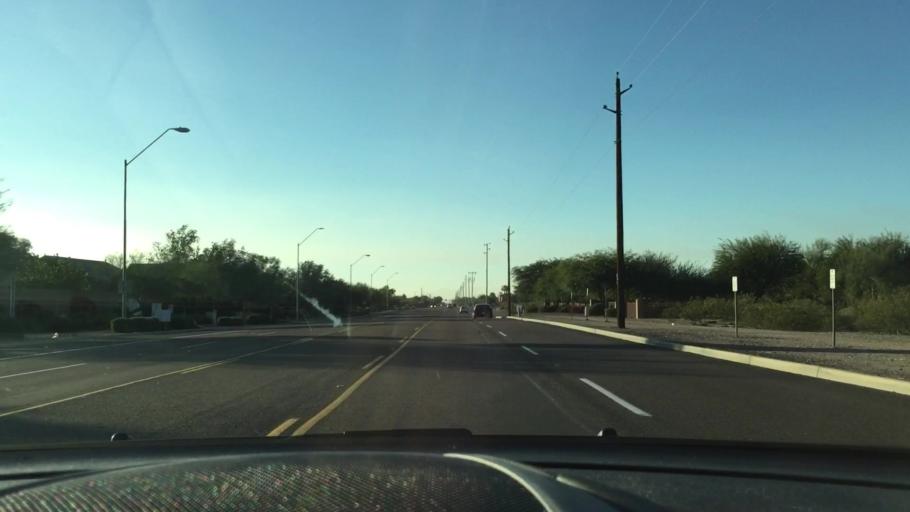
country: US
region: Arizona
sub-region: Maricopa County
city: Sun City
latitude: 33.7051
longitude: -112.2032
